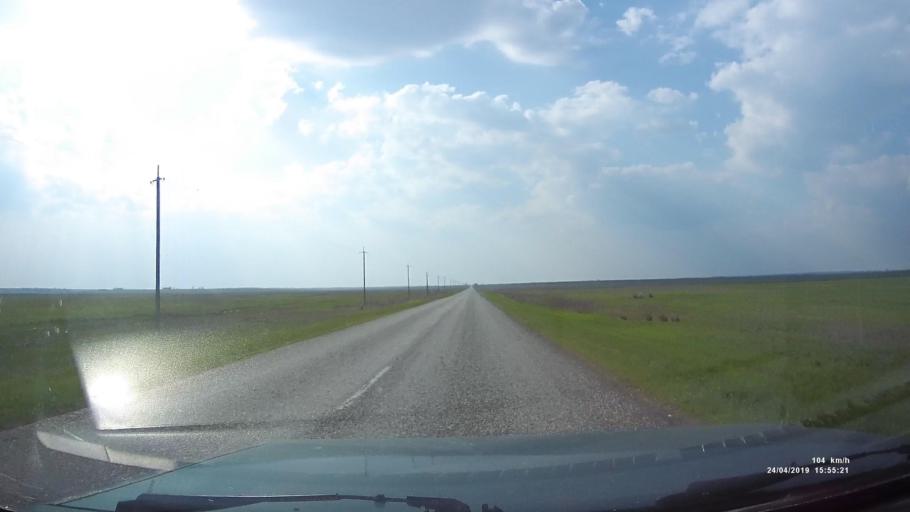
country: RU
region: Kalmykiya
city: Yashalta
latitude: 46.5898
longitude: 42.5509
